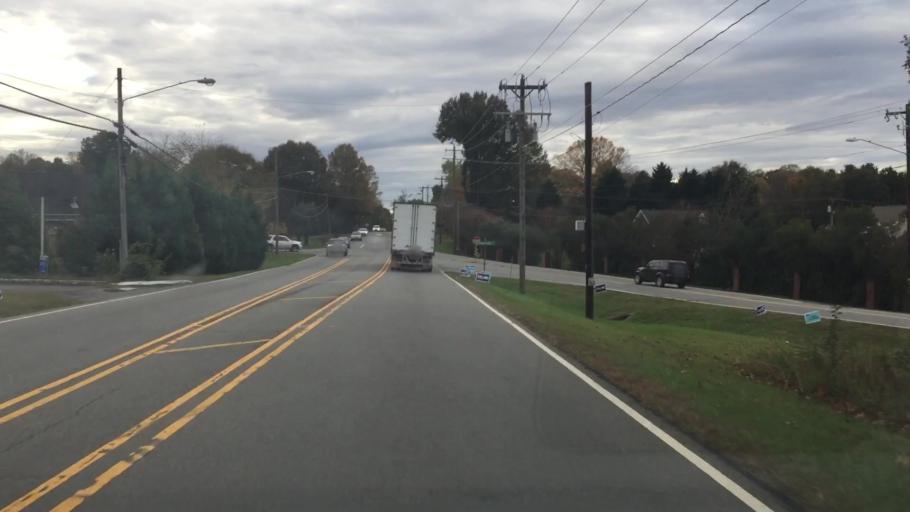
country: US
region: North Carolina
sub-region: Forsyth County
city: Walkertown
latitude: 36.1237
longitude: -80.1789
